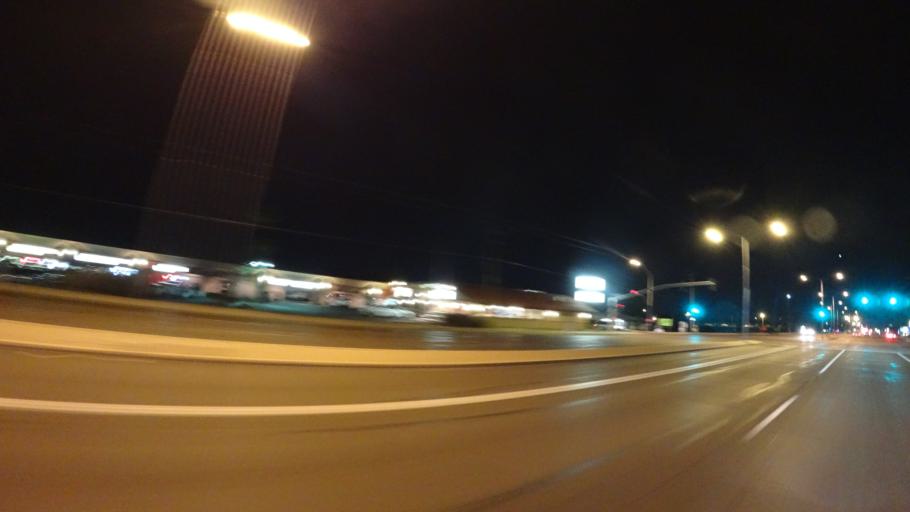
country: US
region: Arizona
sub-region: Maricopa County
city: Gilbert
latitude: 33.4156
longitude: -111.7271
